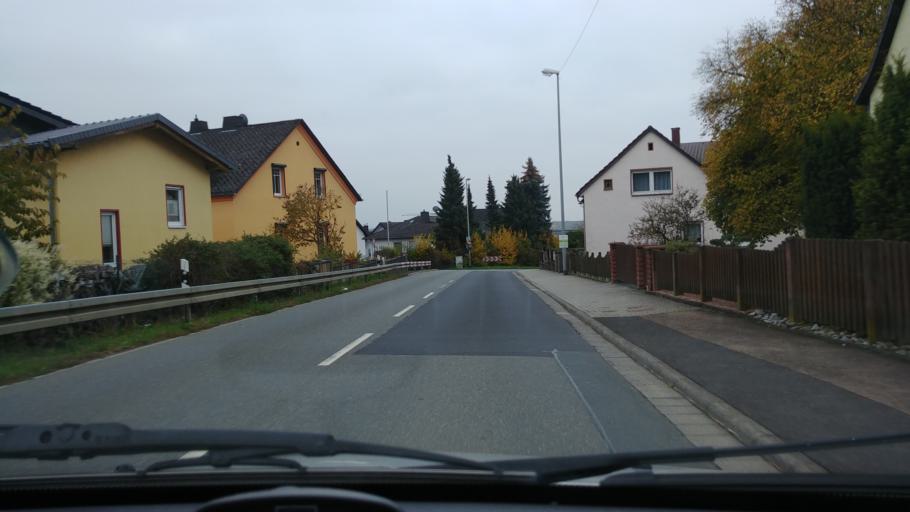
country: DE
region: Hesse
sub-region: Regierungsbezirk Giessen
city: Dehrn
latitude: 50.4262
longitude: 8.0956
